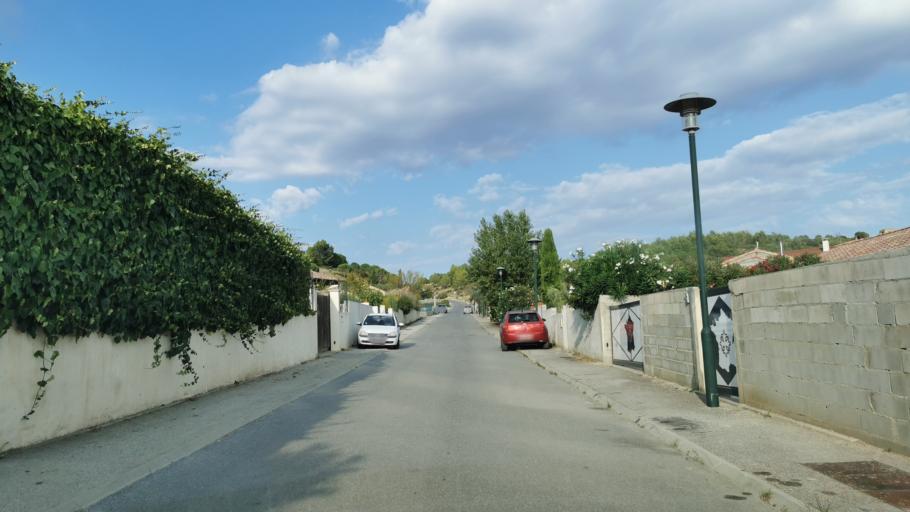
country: FR
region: Languedoc-Roussillon
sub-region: Departement de l'Aude
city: Bizanet
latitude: 43.1686
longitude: 2.8823
